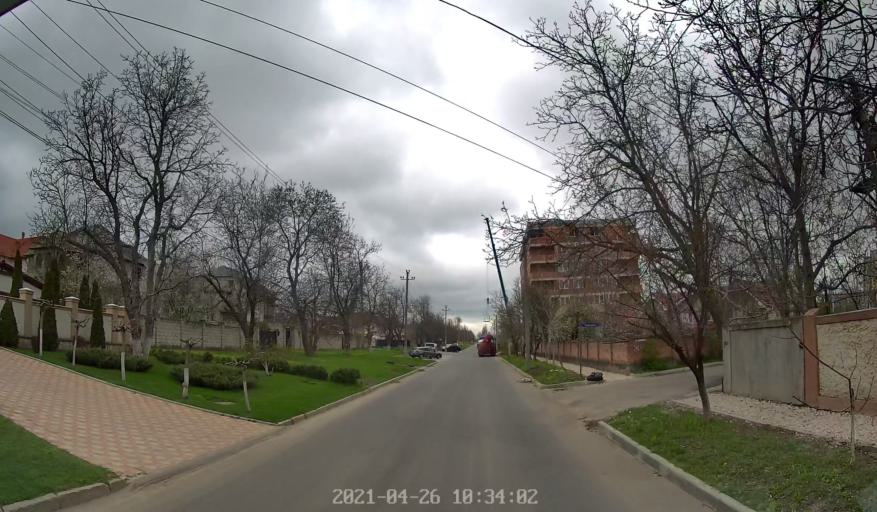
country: MD
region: Chisinau
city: Cricova
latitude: 47.1306
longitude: 28.8620
